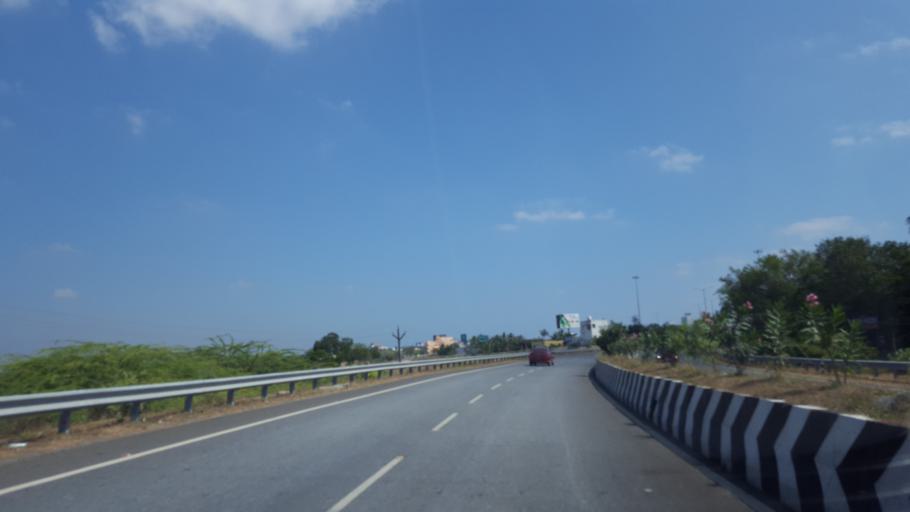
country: IN
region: Tamil Nadu
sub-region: Kancheepuram
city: Mamallapuram
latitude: 12.6265
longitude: 80.1923
